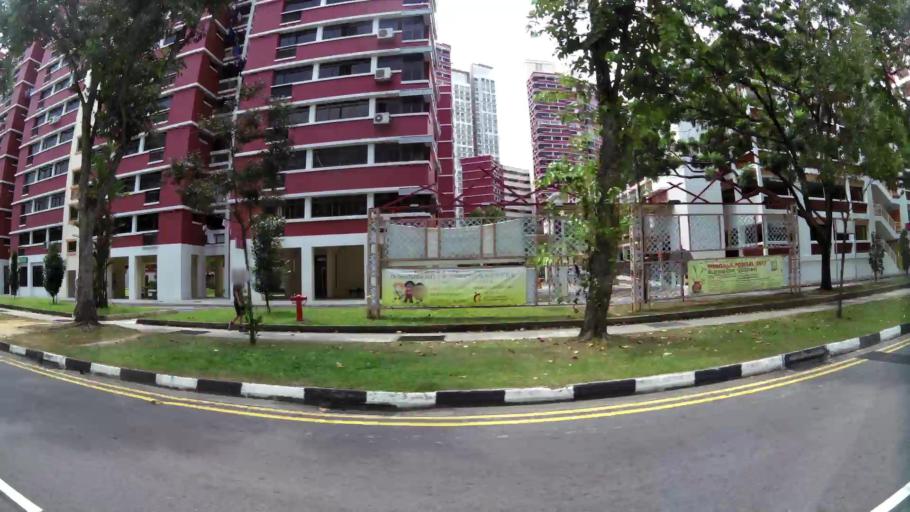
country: SG
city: Singapore
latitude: 1.3466
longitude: 103.7458
